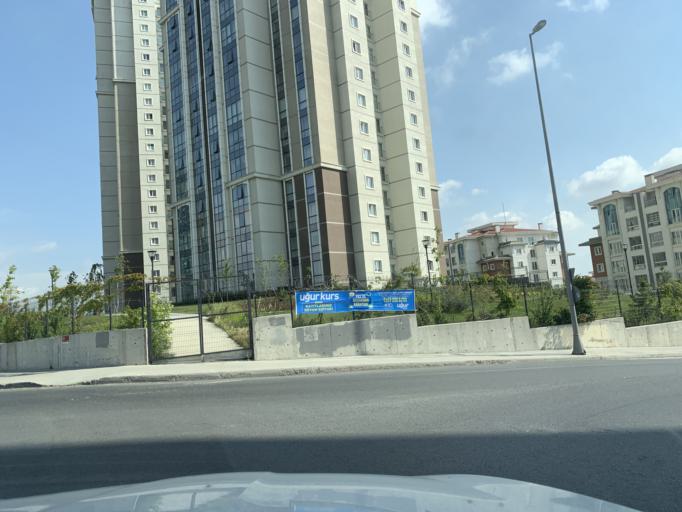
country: TR
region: Istanbul
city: Esenyurt
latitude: 41.0770
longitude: 28.6971
